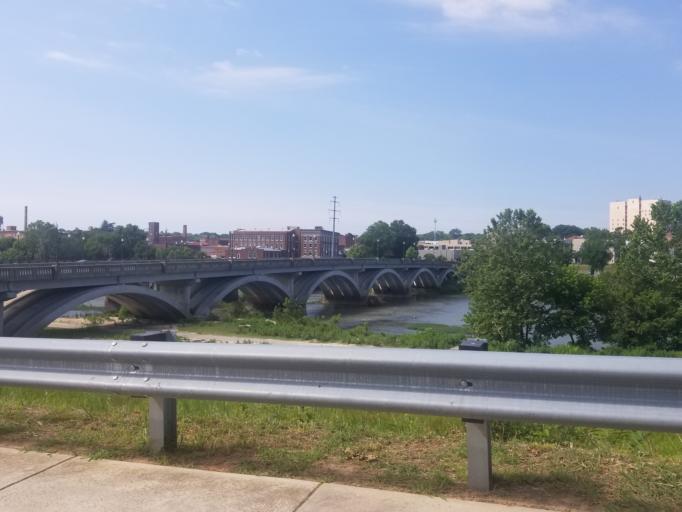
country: US
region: Virginia
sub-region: City of Danville
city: Danville
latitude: 36.5915
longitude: -79.3883
